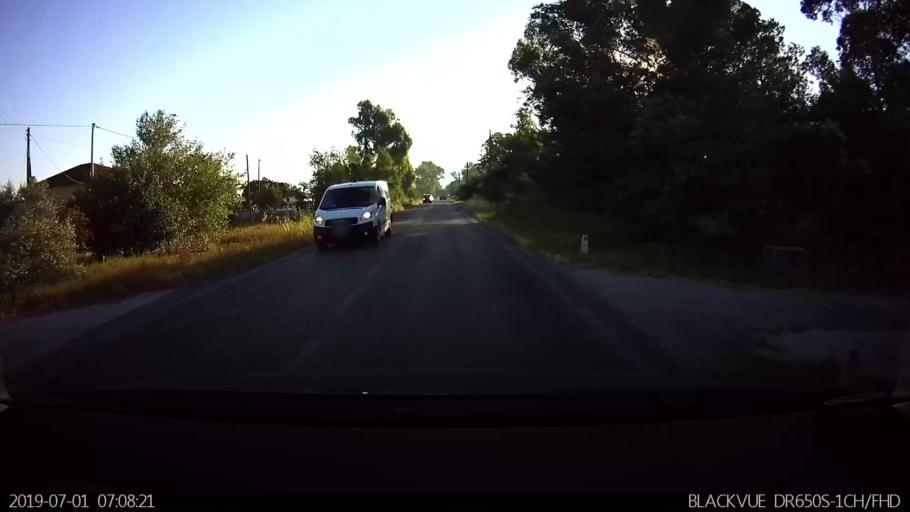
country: IT
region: Latium
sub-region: Provincia di Latina
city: Borgo Hermada
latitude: 41.2965
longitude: 13.1490
